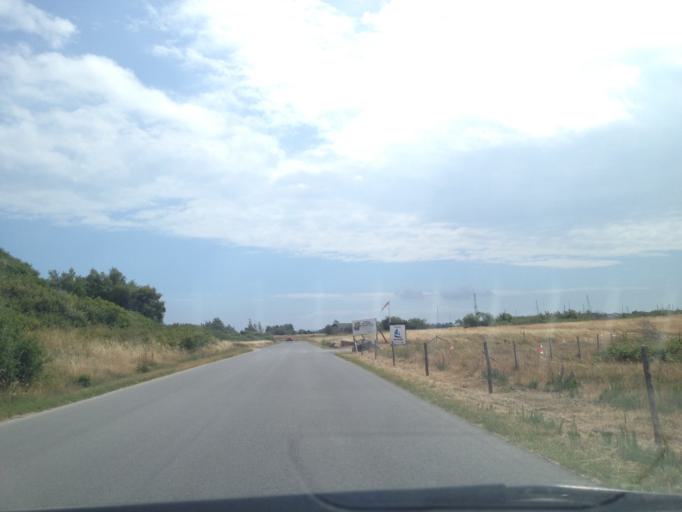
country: DK
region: Central Jutland
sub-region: Syddjurs Kommune
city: Ebeltoft
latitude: 56.1545
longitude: 10.6858
